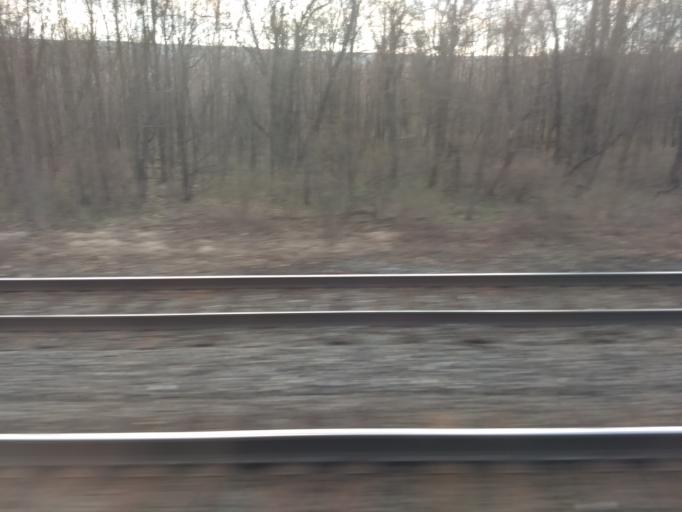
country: US
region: Pennsylvania
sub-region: Blair County
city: Bellwood
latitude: 40.5866
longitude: -78.3457
